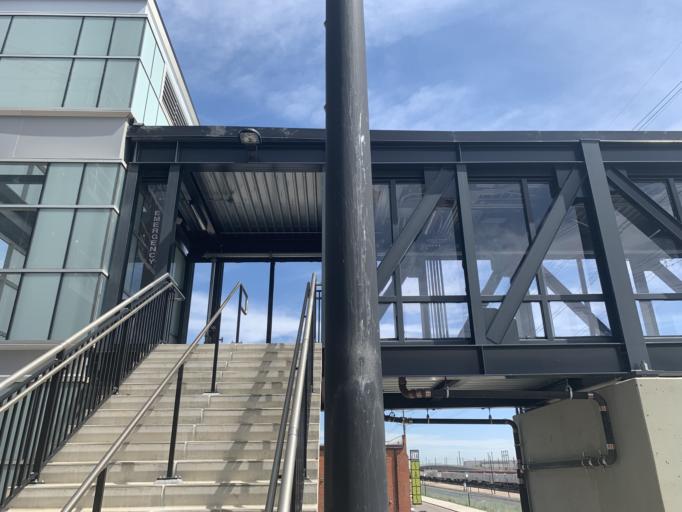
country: US
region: Colorado
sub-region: Denver County
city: Denver
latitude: 39.7727
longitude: -104.9985
